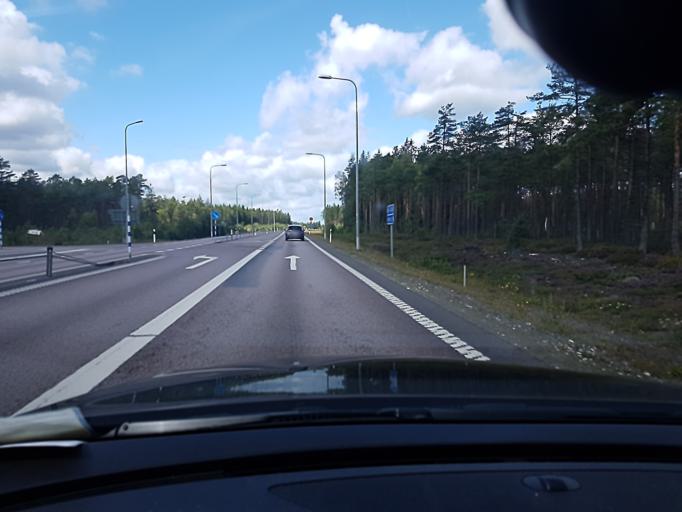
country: SE
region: Kalmar
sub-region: Emmaboda Kommun
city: Emmaboda
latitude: 56.7250
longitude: 15.5777
